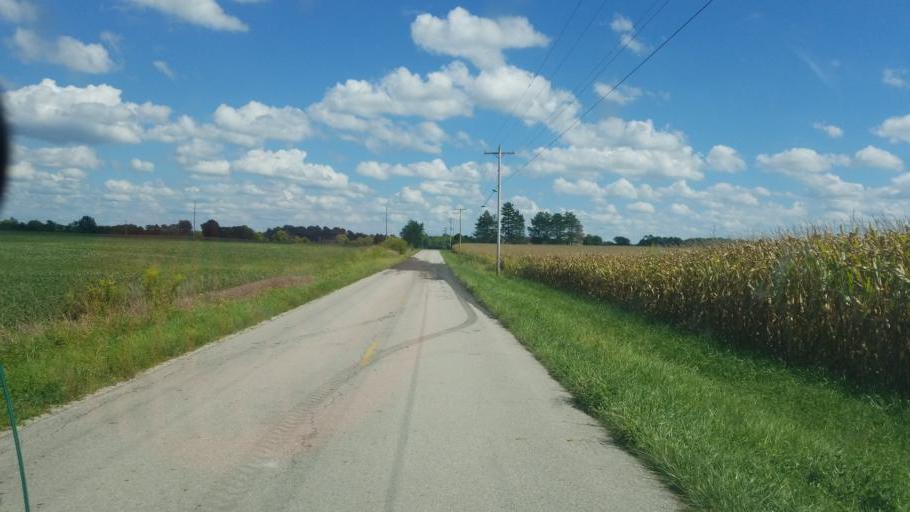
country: US
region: Ohio
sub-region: Delaware County
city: Delaware
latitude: 40.3110
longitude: -83.2044
